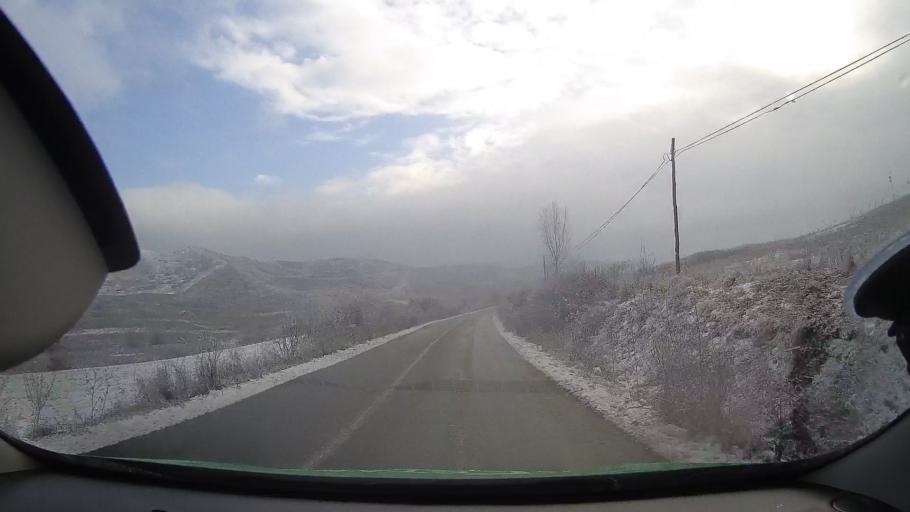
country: RO
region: Mures
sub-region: Comuna Chetani
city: Chetani
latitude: 46.4238
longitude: 24.0145
